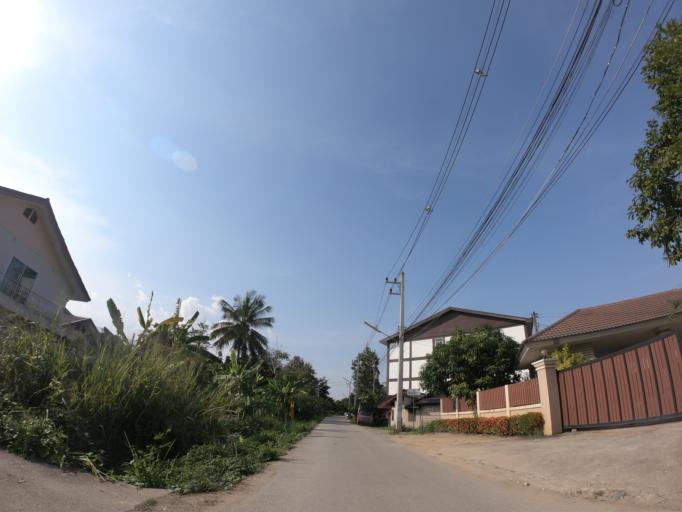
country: TH
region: Chiang Mai
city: Chiang Mai
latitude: 18.8288
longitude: 98.9914
